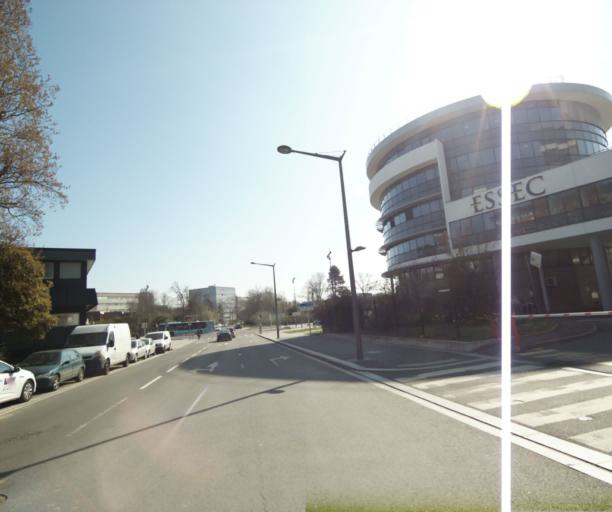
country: FR
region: Ile-de-France
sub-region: Departement du Val-d'Oise
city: Cergy
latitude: 49.0336
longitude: 2.0785
